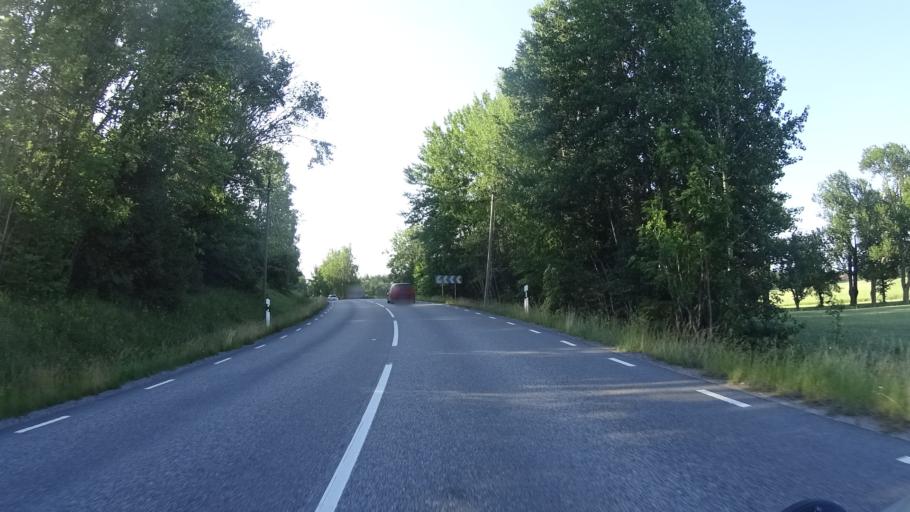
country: SE
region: Stockholm
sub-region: Sodertalje Kommun
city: Pershagen
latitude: 59.1119
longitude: 17.6432
